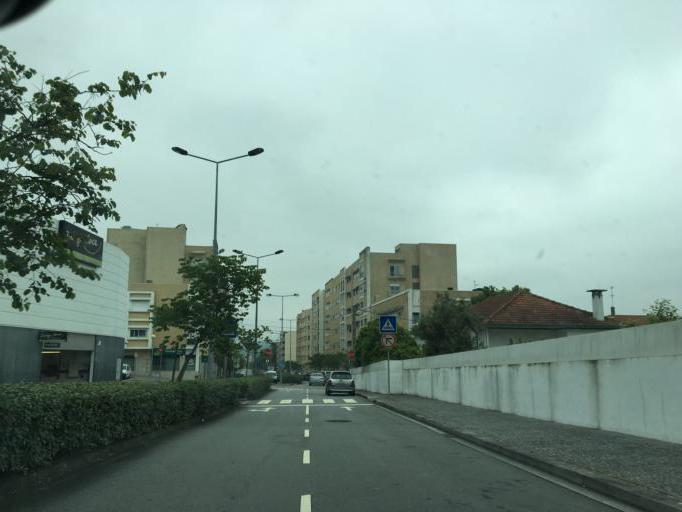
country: PT
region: Porto
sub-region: Maia
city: Anta
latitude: 41.2645
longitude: -8.6147
